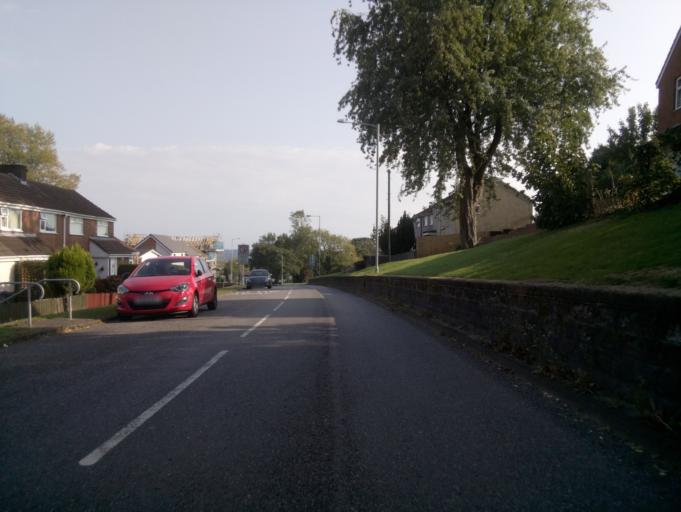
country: GB
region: Wales
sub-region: Torfaen County Borough
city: Cwmbran
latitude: 51.6629
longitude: -3.0406
